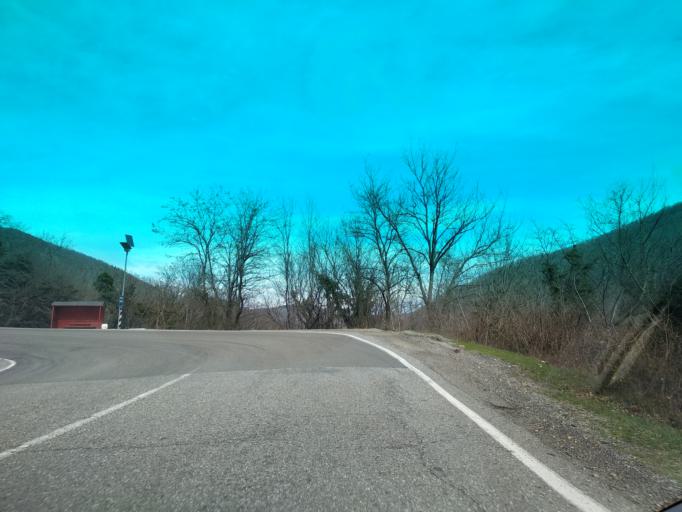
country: RU
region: Krasnodarskiy
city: Shepsi
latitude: 44.0729
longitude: 39.1401
